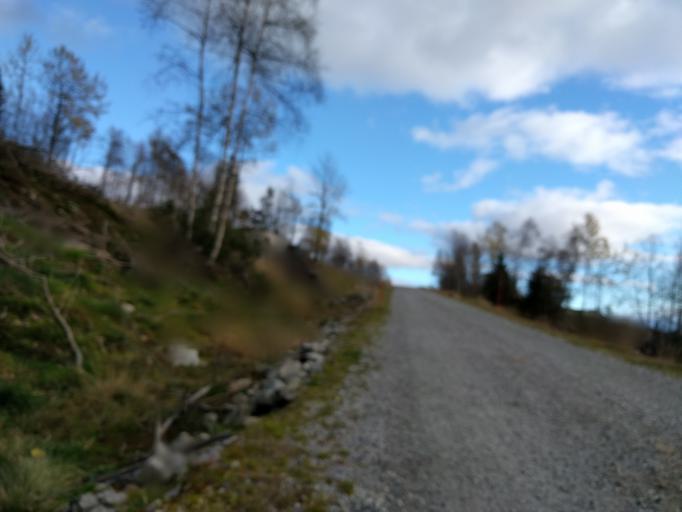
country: NO
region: Aust-Agder
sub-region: Evje og Hornnes
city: Evje
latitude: 58.6534
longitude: 7.9467
